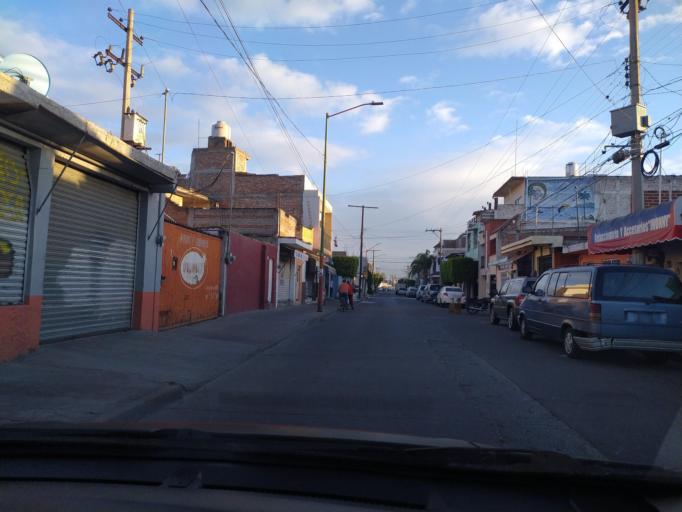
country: MX
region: Guanajuato
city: San Francisco del Rincon
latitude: 21.0119
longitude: -101.8524
